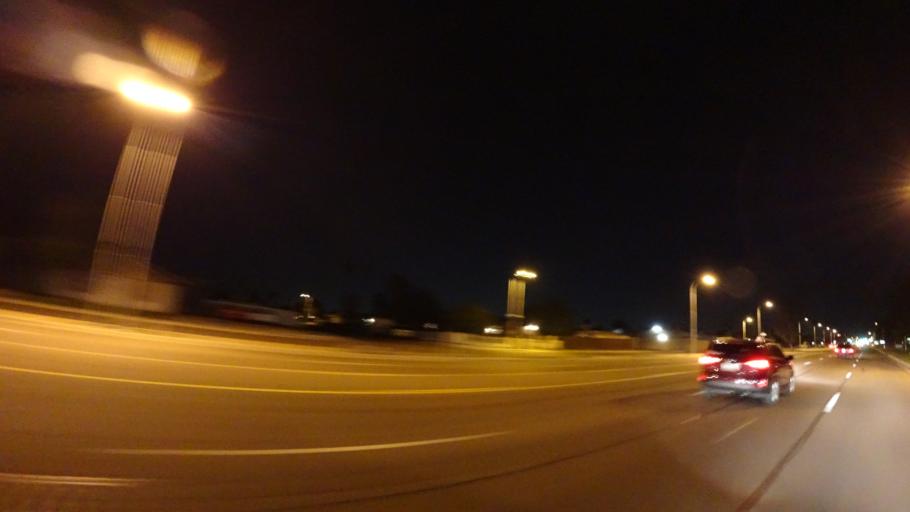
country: US
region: Arizona
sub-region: Maricopa County
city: Guadalupe
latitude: 33.3950
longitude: -111.9783
